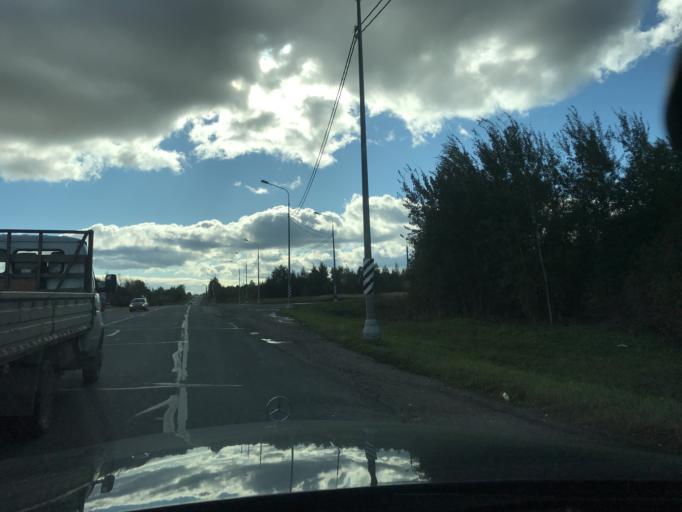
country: RU
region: Pskov
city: Ostrov
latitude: 57.3324
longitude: 28.3694
